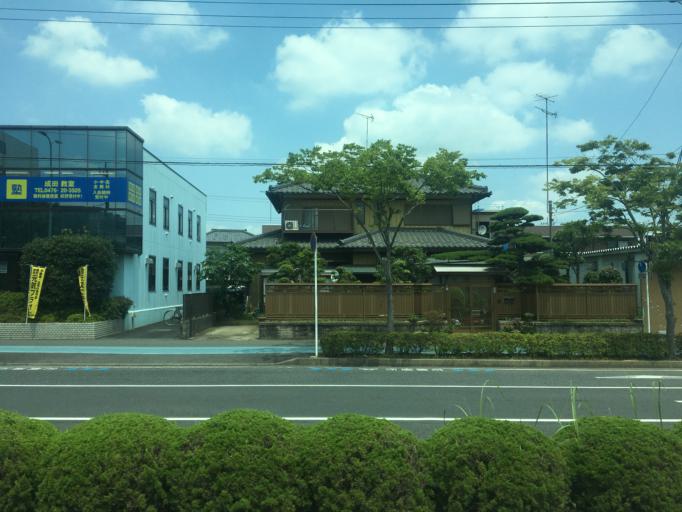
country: JP
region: Chiba
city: Narita
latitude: 35.7781
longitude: 140.3108
